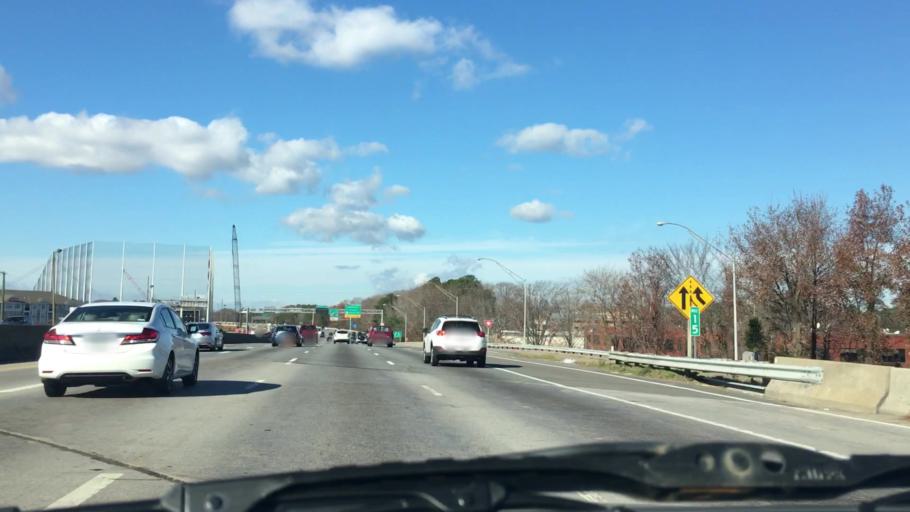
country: US
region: Virginia
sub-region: City of Chesapeake
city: Chesapeake
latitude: 36.8407
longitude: -76.1625
